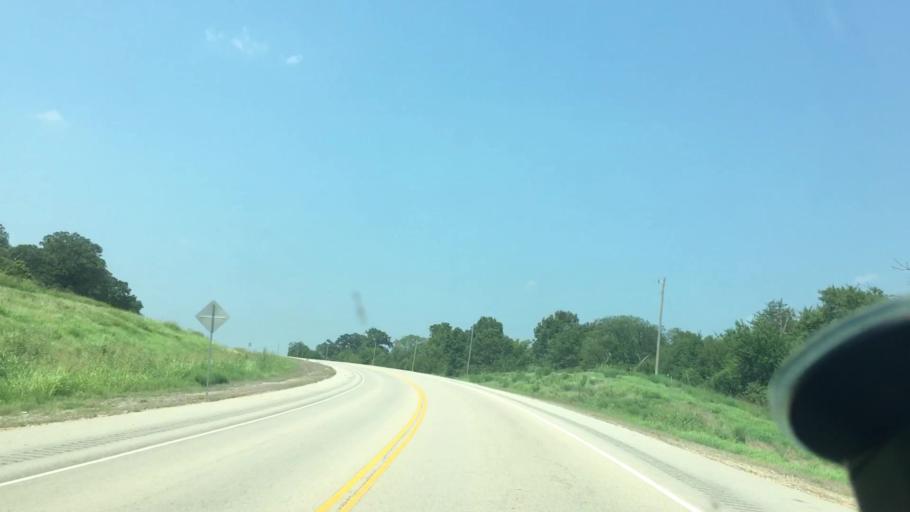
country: US
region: Oklahoma
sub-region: Atoka County
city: Atoka
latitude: 34.2872
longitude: -95.9599
